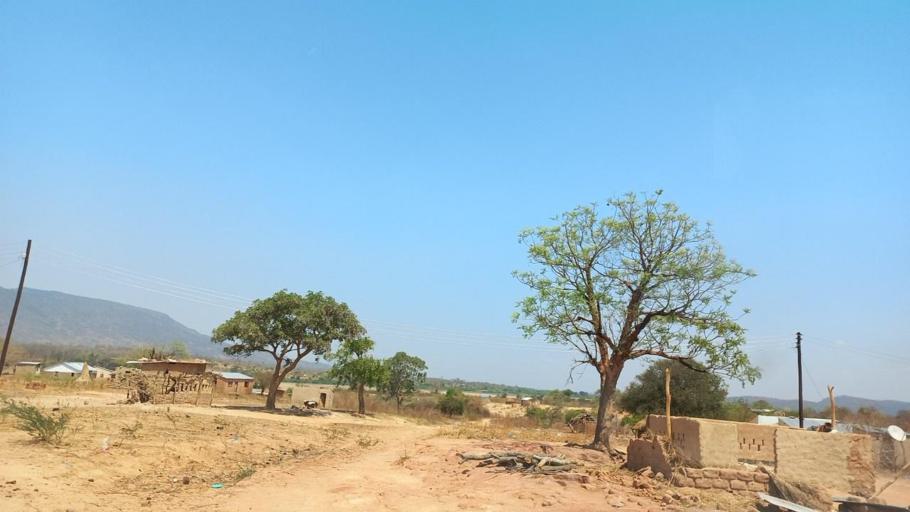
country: ZM
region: Lusaka
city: Luangwa
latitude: -15.5907
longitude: 30.3968
